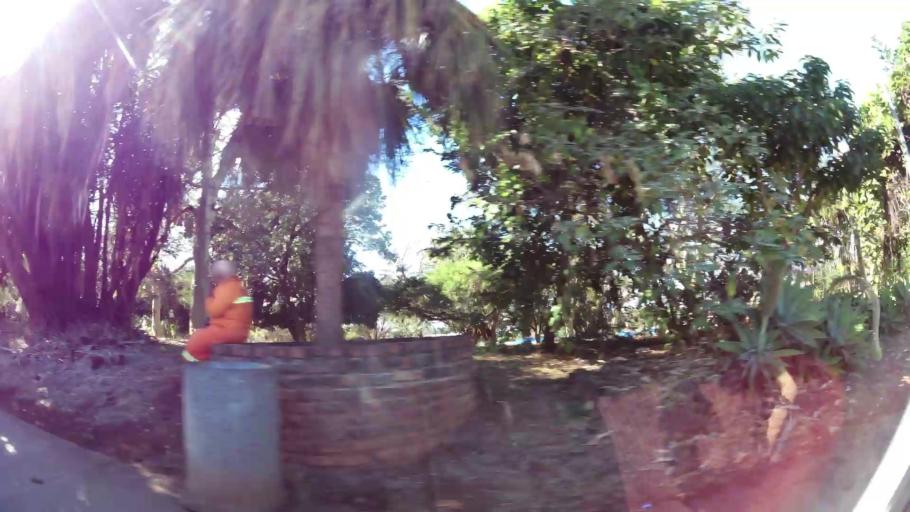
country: ZA
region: Limpopo
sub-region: Mopani District Municipality
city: Tzaneen
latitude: -23.8225
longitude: 30.1589
